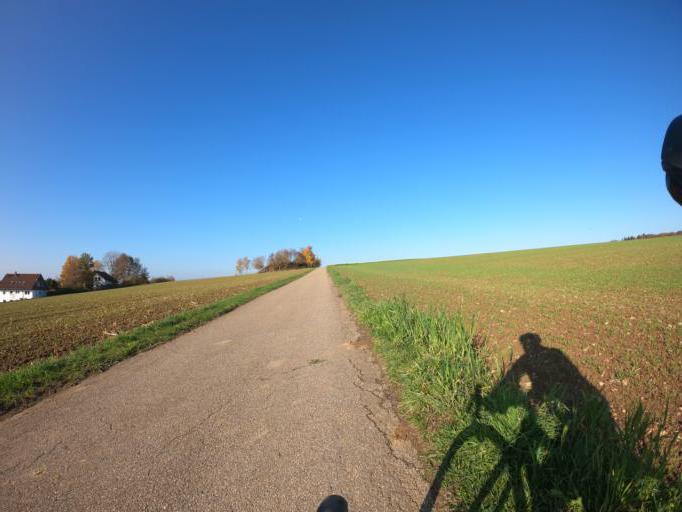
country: DE
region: Baden-Wuerttemberg
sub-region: Regierungsbezirk Stuttgart
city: Aidlingen
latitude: 48.7207
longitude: 8.9098
